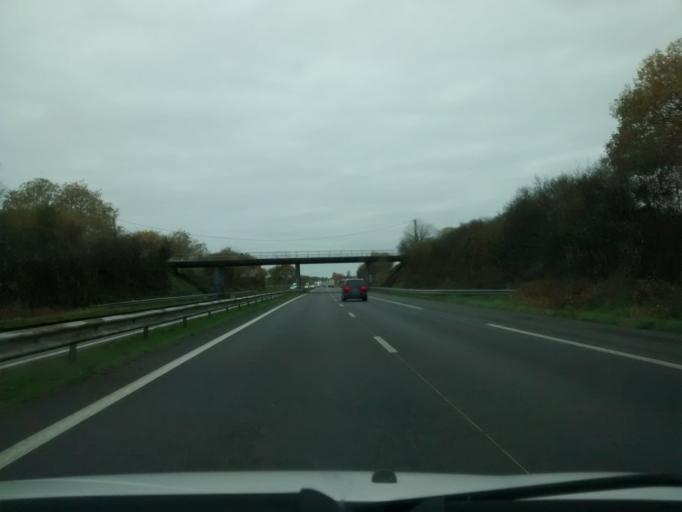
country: FR
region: Brittany
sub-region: Departement d'Ille-et-Vilaine
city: Chateaubourg
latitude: 48.0947
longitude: -1.3997
